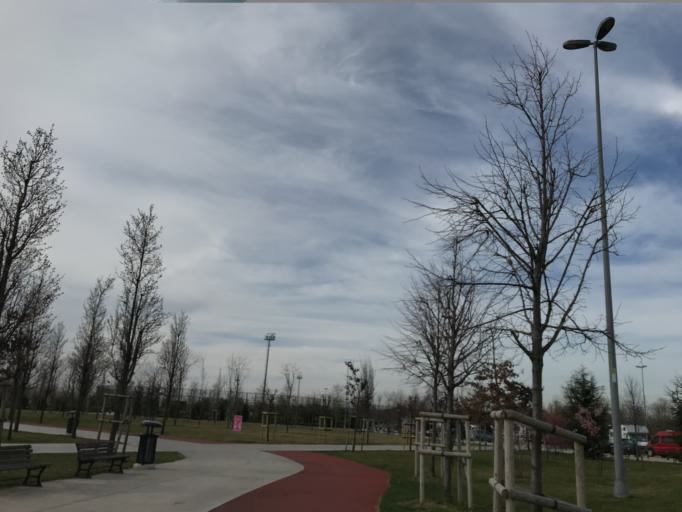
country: TR
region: Istanbul
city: Maltepe
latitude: 40.9373
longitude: 29.1118
